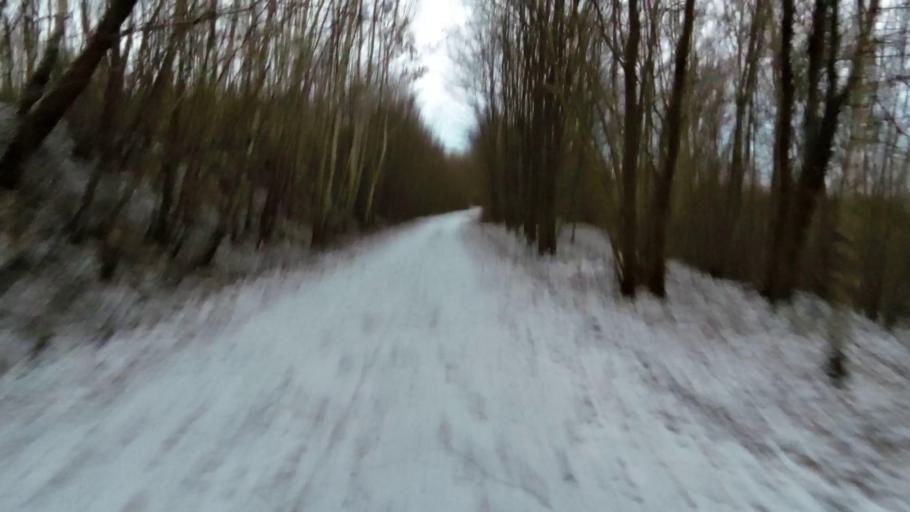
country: PL
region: West Pomeranian Voivodeship
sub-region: Powiat swidwinski
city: Polczyn-Zdroj
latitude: 53.7444
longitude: 16.0585
